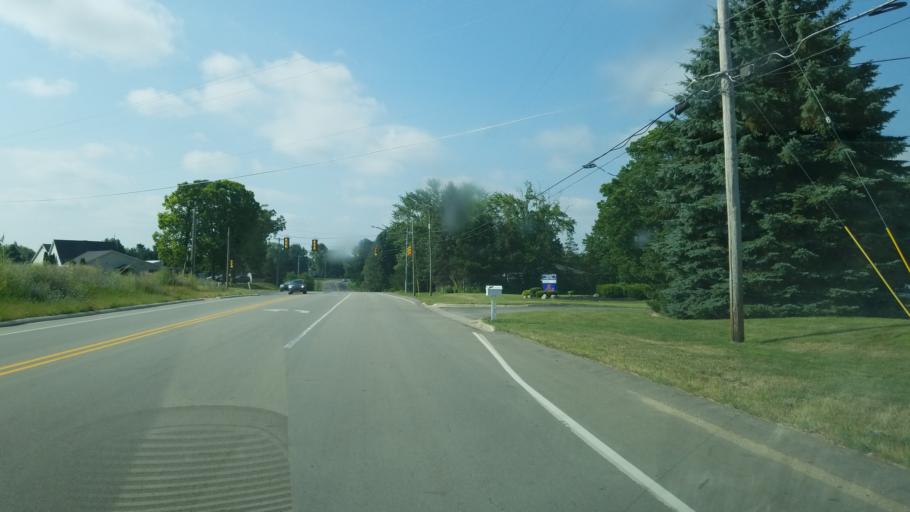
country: US
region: Michigan
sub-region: Kent County
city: Northview
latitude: 43.0957
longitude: -85.6390
